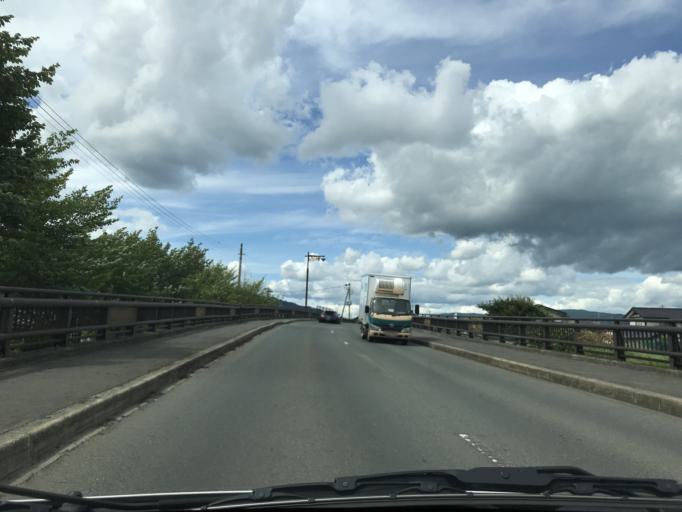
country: JP
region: Iwate
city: Tono
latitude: 39.3308
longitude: 141.5368
